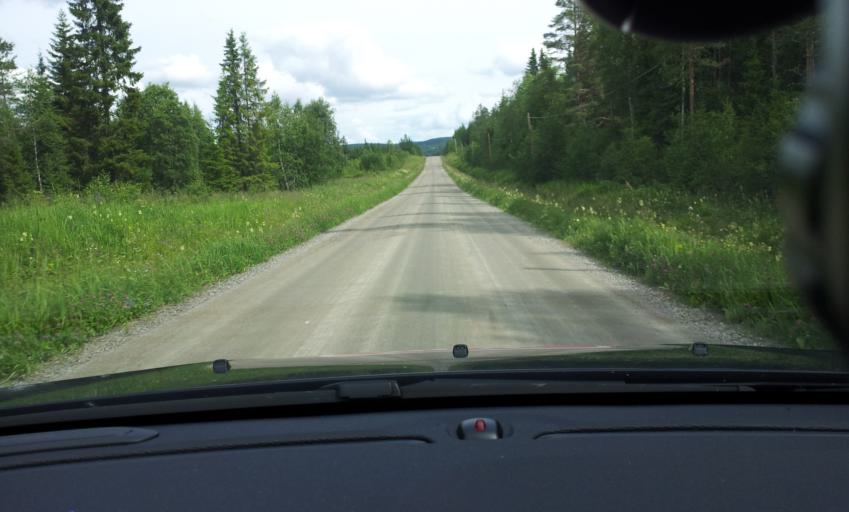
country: SE
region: Jaemtland
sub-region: OEstersunds Kommun
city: Brunflo
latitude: 62.9472
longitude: 14.9856
